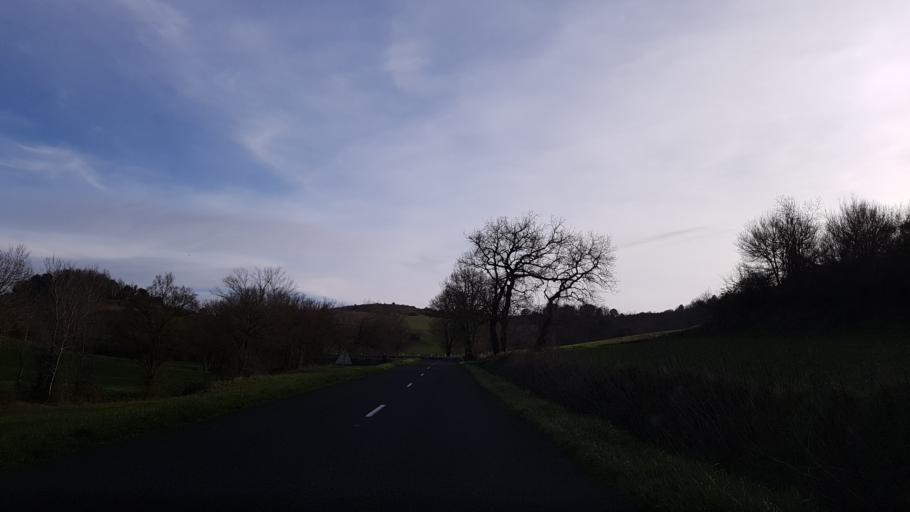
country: FR
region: Midi-Pyrenees
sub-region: Departement de l'Ariege
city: Mirepoix
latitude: 43.1367
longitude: 1.9108
